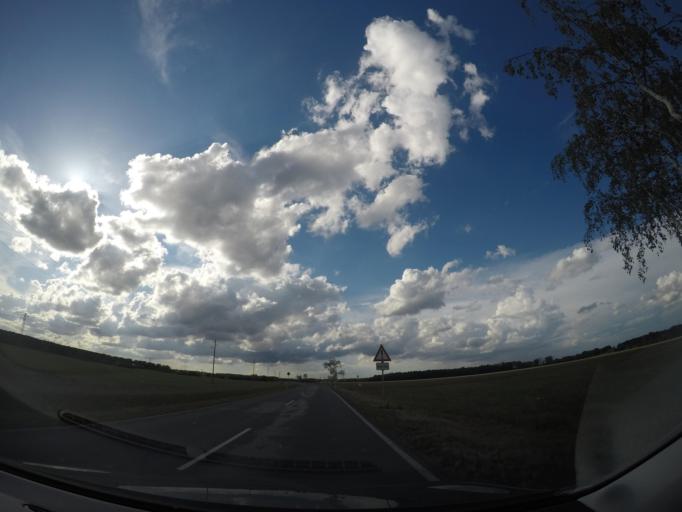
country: DE
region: Saxony-Anhalt
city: Haldensleben I
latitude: 52.3012
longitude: 11.3924
